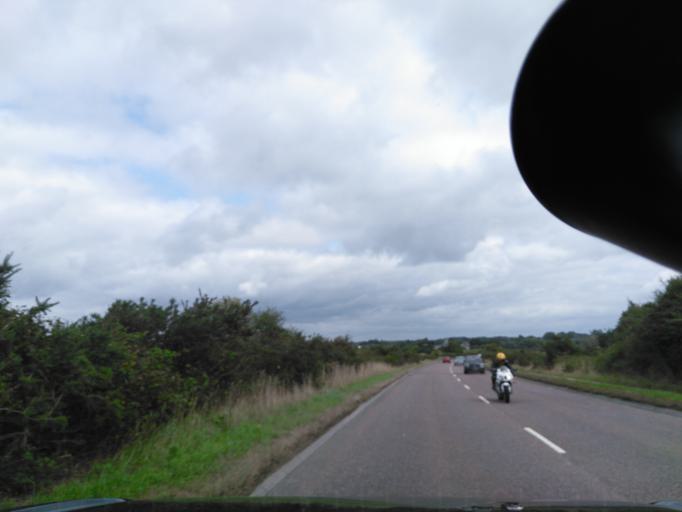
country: GB
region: England
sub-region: Dorset
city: Wareham
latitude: 50.6857
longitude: -2.1239
